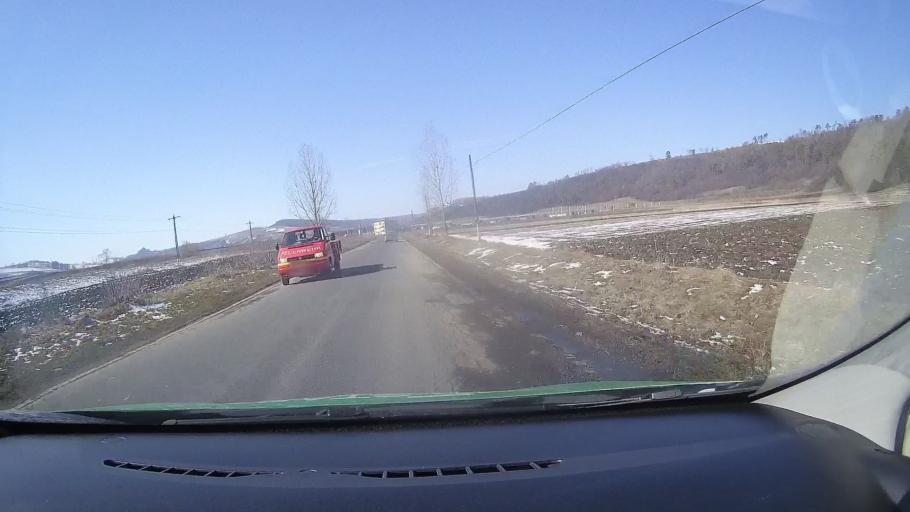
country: RO
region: Brasov
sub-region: Comuna Homorod
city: Homorod
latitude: 46.0385
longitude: 25.2623
